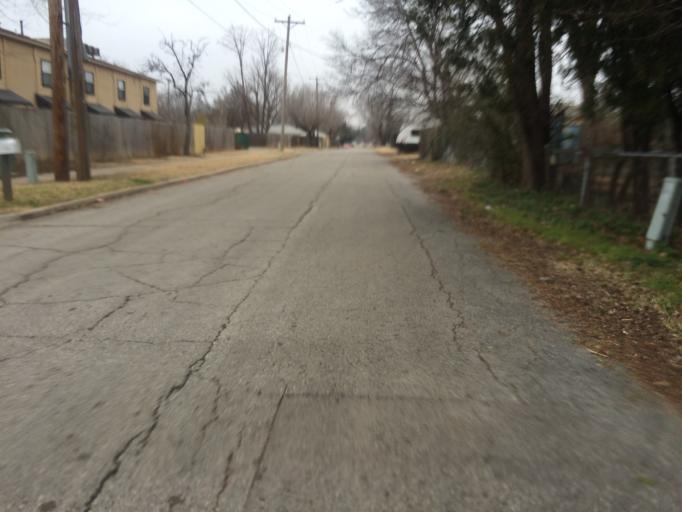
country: US
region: Oklahoma
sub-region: Cleveland County
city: Norman
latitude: 35.2062
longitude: -97.4280
